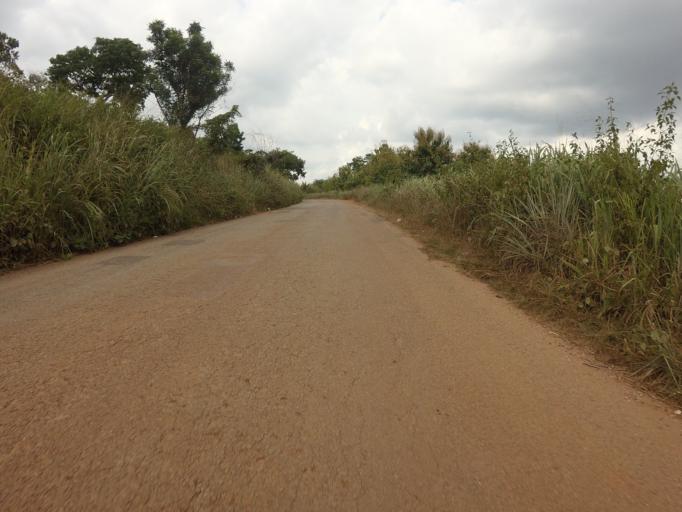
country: GH
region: Volta
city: Ho
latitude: 6.6768
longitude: 0.3523
